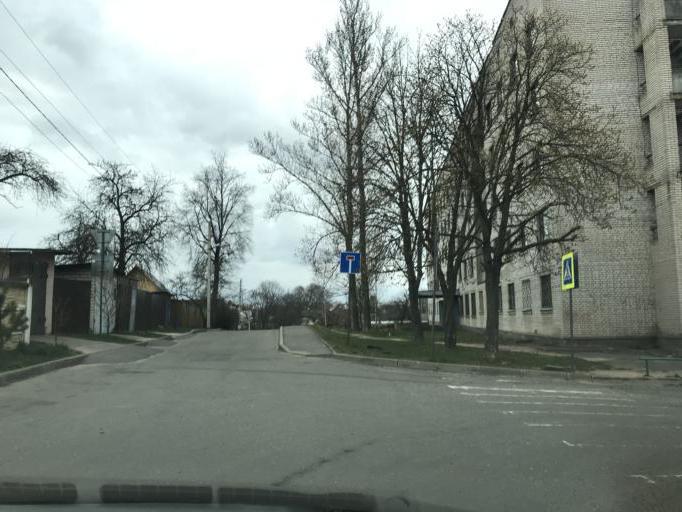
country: BY
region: Mogilev
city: Mahilyow
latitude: 53.8992
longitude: 30.3215
